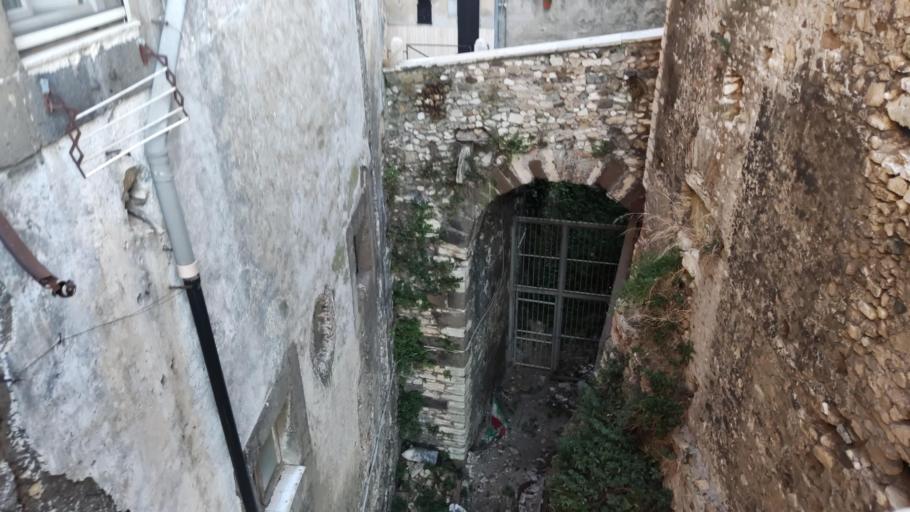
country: IT
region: Latium
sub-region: Citta metropolitana di Roma Capitale
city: Tivoli
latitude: 41.9663
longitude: 12.8000
